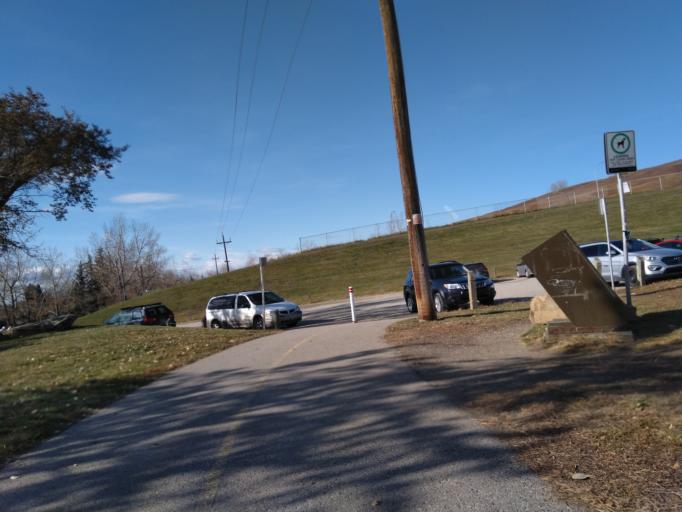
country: CA
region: Alberta
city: Calgary
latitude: 51.0918
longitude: -114.1056
